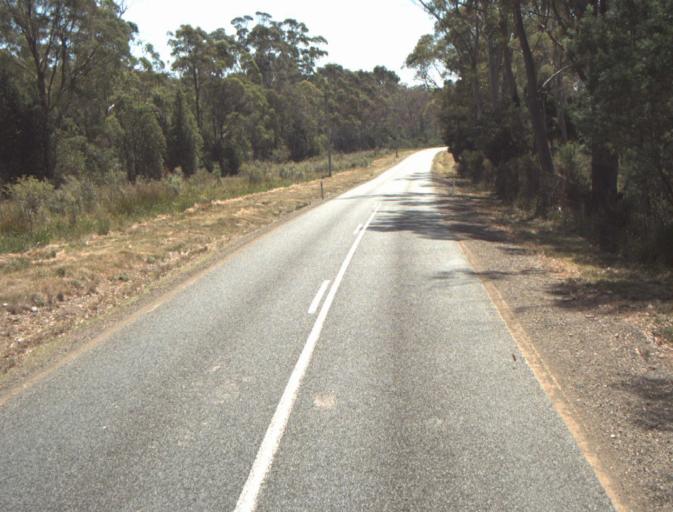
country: AU
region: Tasmania
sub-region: Launceston
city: Mayfield
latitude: -41.3358
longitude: 147.1425
